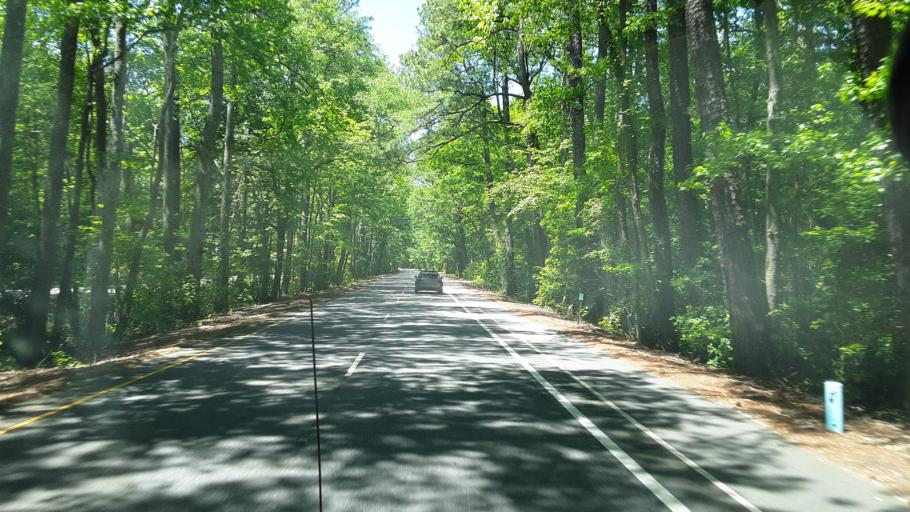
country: US
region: Virginia
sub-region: City of Virginia Beach
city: Virginia Beach
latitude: 36.9176
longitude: -76.0170
